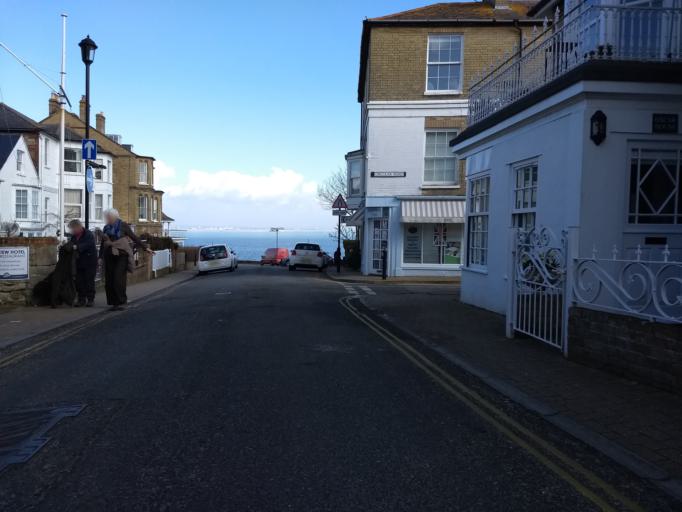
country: GB
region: England
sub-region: Isle of Wight
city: Seaview
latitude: 50.7204
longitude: -1.1098
